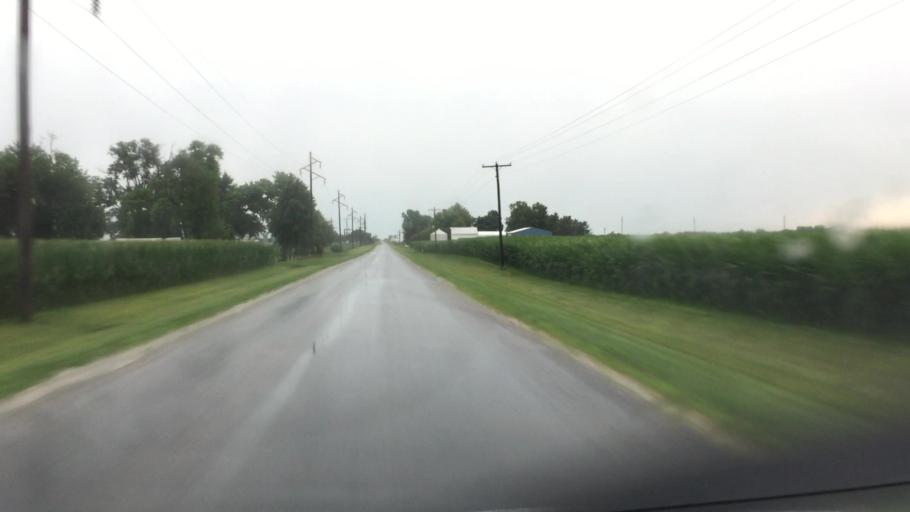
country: US
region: Illinois
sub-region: Hancock County
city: Hamilton
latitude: 40.4299
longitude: -91.2715
